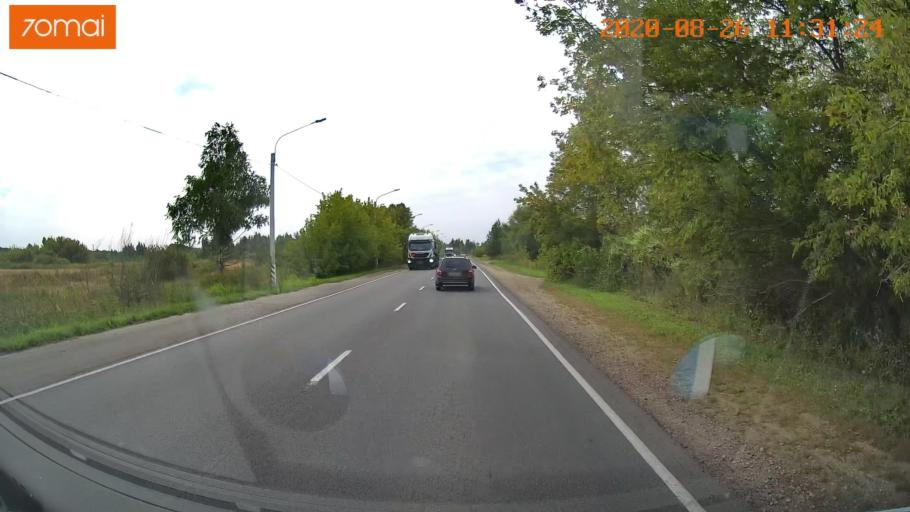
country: RU
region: Rjazan
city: Shilovo
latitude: 54.3066
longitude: 40.8742
